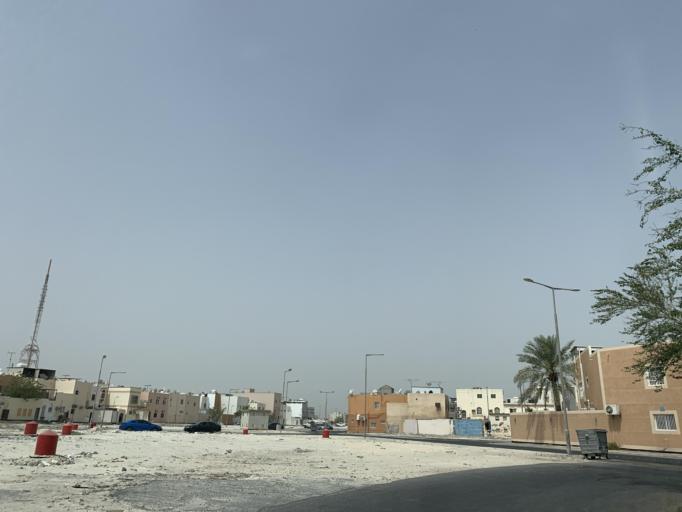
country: BH
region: Northern
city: Madinat `Isa
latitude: 26.1648
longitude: 50.5589
